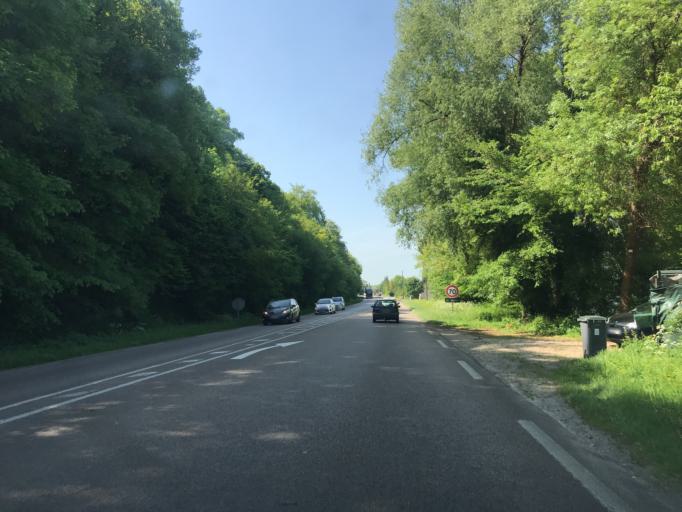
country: FR
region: Haute-Normandie
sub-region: Departement de la Seine-Maritime
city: Les Authieux-sur-le-Port-Saint-Ouen
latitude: 49.3423
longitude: 1.1235
